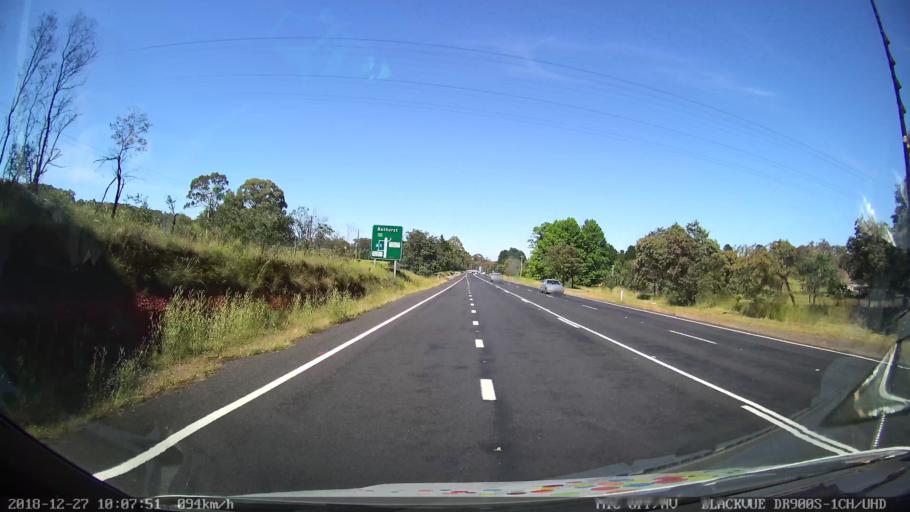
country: AU
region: New South Wales
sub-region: Lithgow
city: Portland
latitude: -33.4434
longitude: 149.8341
